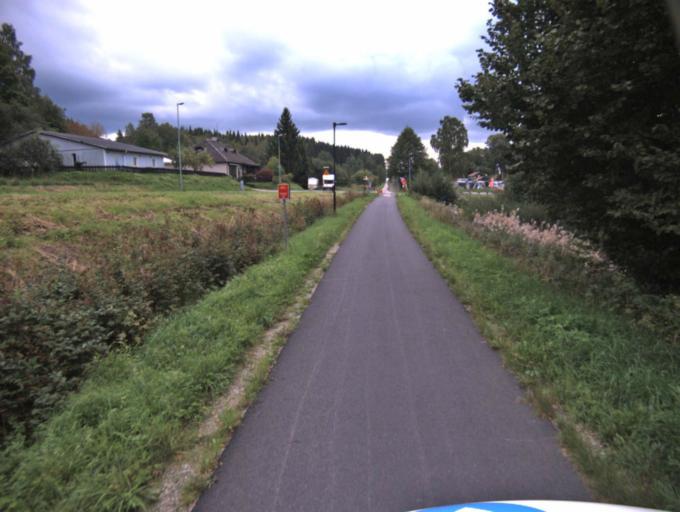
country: SE
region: Vaestra Goetaland
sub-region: Ulricehamns Kommun
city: Ulricehamn
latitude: 57.7717
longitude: 13.4033
